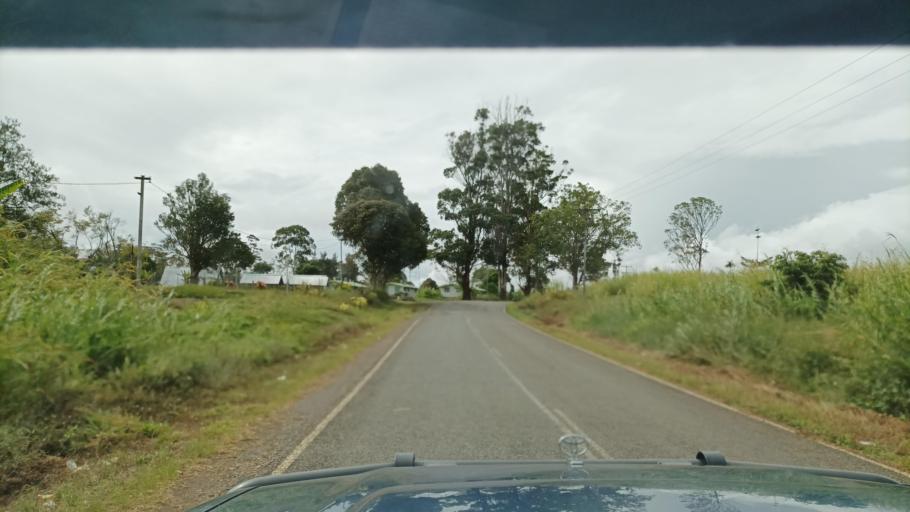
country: PG
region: Jiwaka
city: Minj
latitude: -5.8986
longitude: 144.6849
